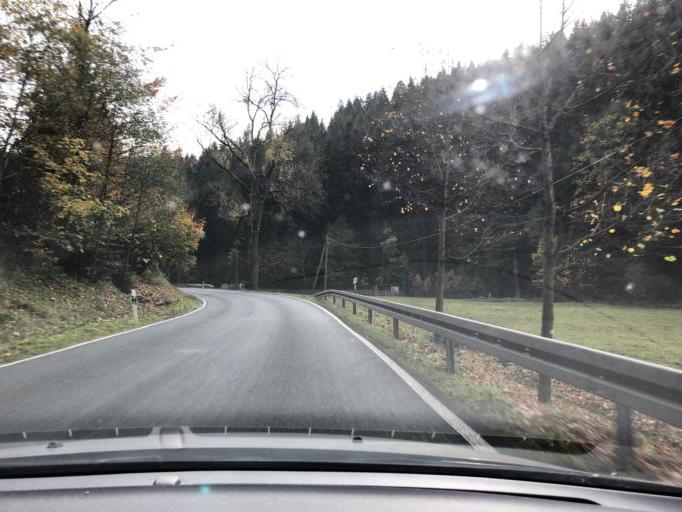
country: DE
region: Thuringia
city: Katzhutte
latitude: 50.5409
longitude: 11.0648
